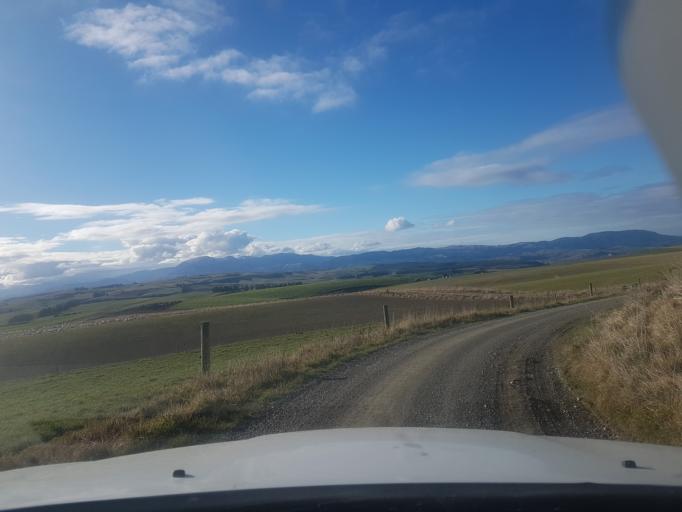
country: NZ
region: Canterbury
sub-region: Timaru District
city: Pleasant Point
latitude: -44.1729
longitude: 170.8884
